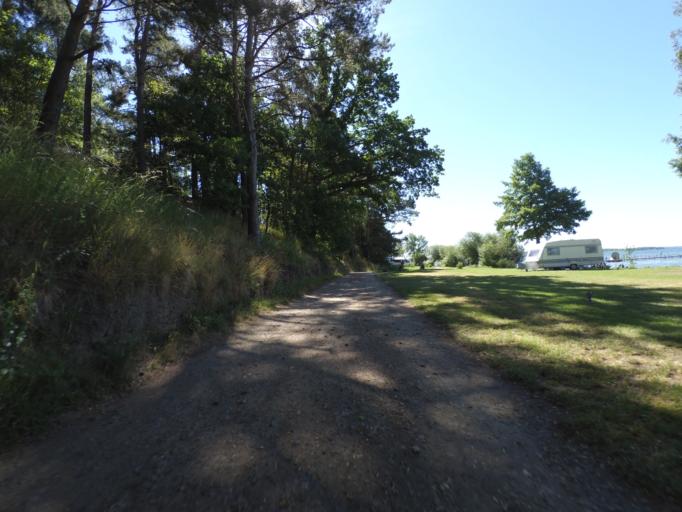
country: DE
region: Mecklenburg-Vorpommern
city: Plau am See
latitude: 53.5219
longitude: 12.3203
